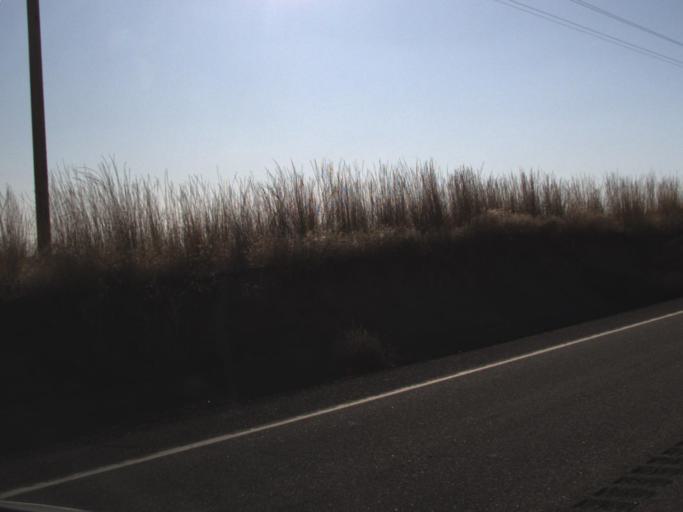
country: US
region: Washington
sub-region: Walla Walla County
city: Garrett
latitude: 46.2963
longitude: -118.6180
